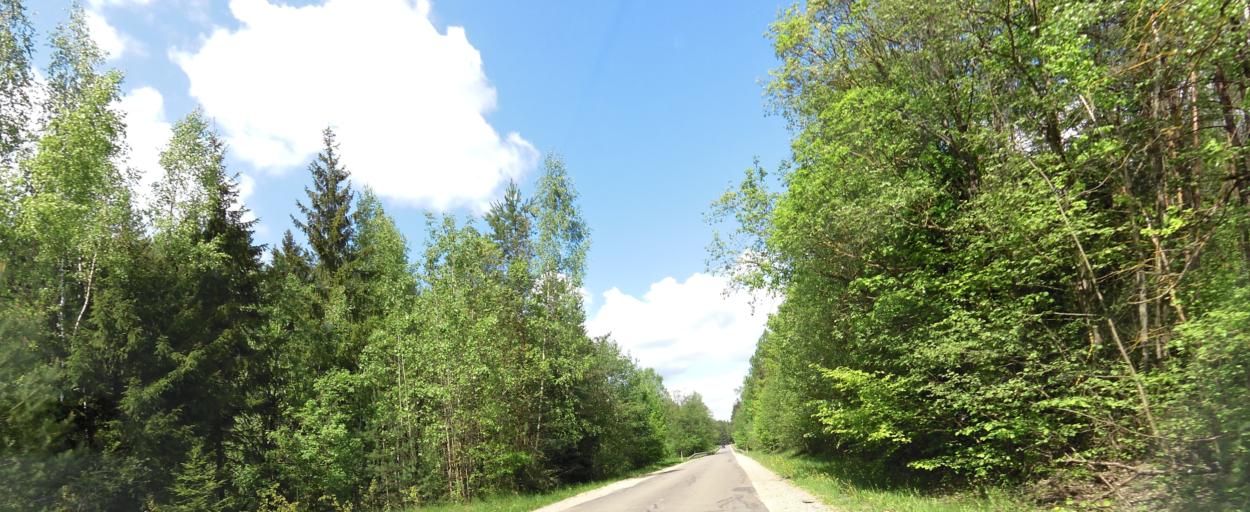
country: LT
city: Trakai
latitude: 54.6989
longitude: 24.9655
